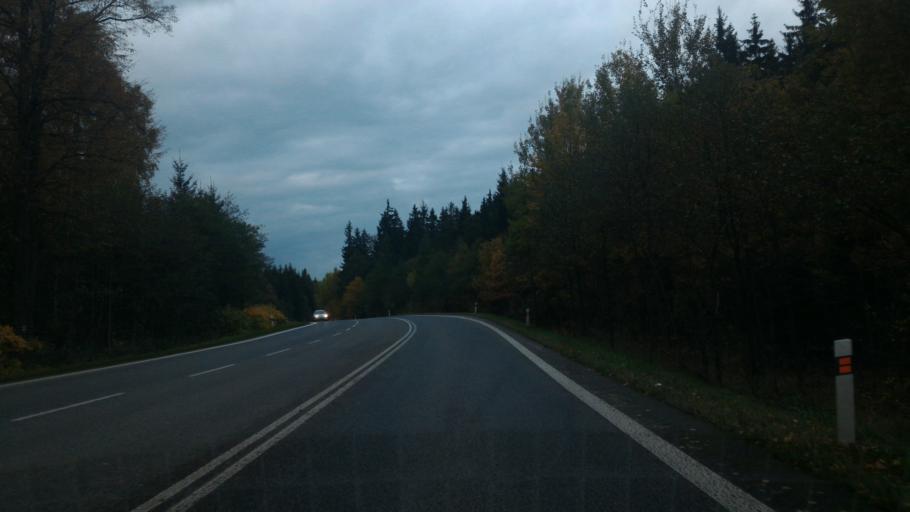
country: CZ
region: Ustecky
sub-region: Okres Decin
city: Rumburk
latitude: 50.9232
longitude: 14.5619
